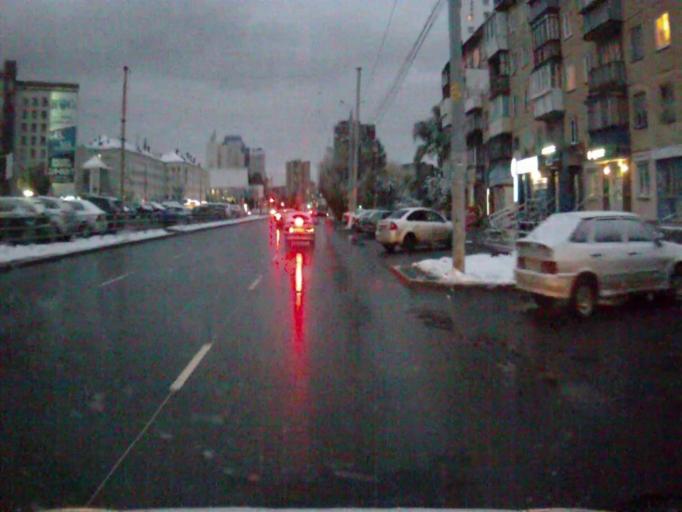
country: RU
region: Chelyabinsk
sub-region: Gorod Chelyabinsk
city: Chelyabinsk
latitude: 55.1491
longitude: 61.3921
